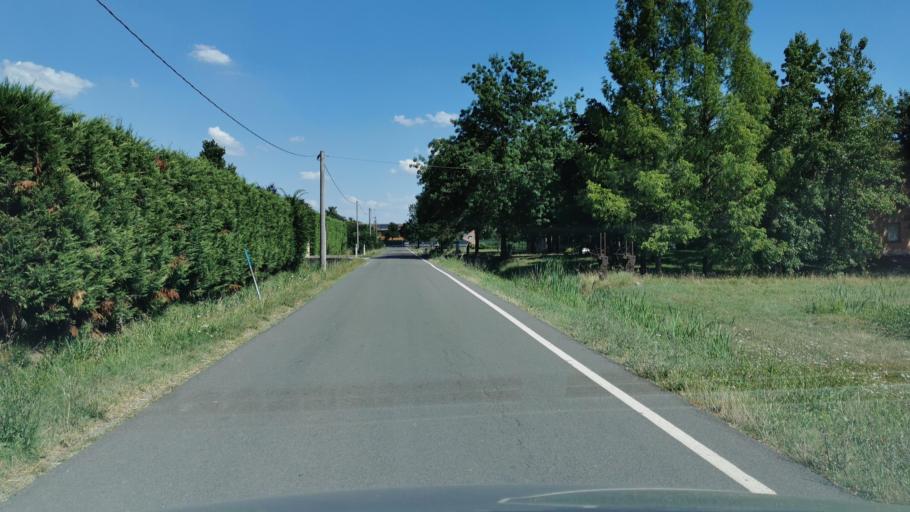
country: IT
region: Emilia-Romagna
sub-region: Provincia di Modena
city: Limidi
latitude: 44.7823
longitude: 10.9165
